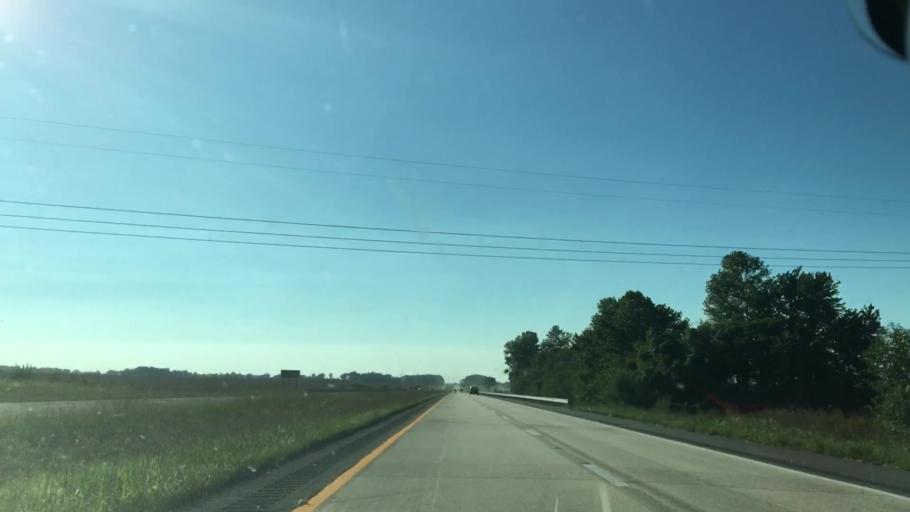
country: US
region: Kentucky
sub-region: Henderson County
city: Henderson
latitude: 37.7992
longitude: -87.5101
